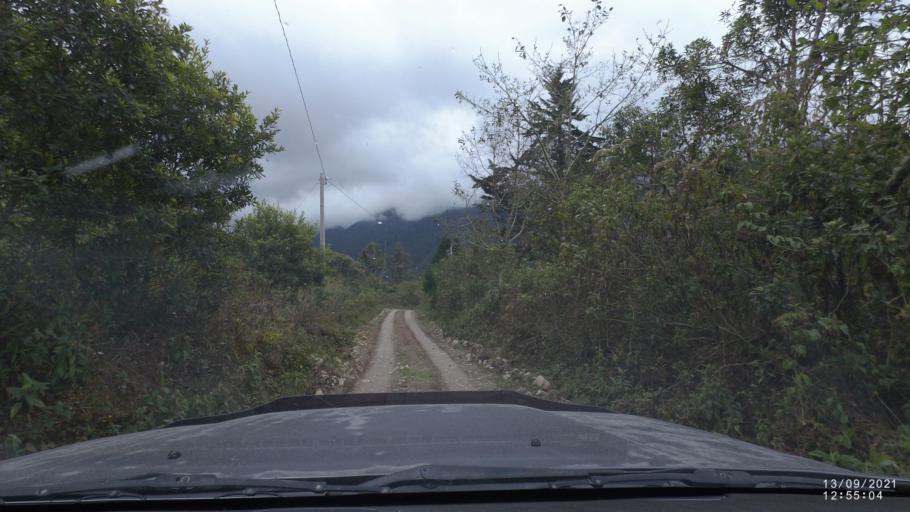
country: BO
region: Cochabamba
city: Colomi
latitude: -17.2426
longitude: -65.8218
